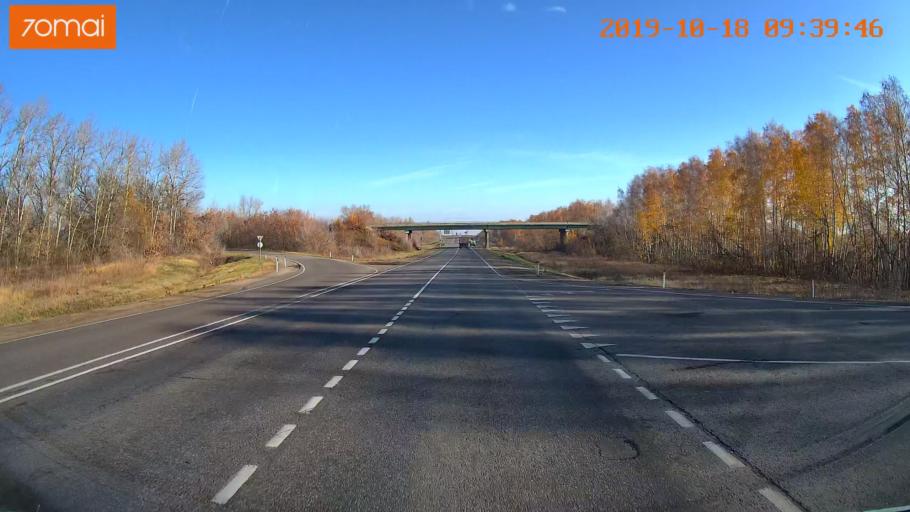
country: RU
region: Tula
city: Yefremov
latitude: 53.2568
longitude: 38.1392
